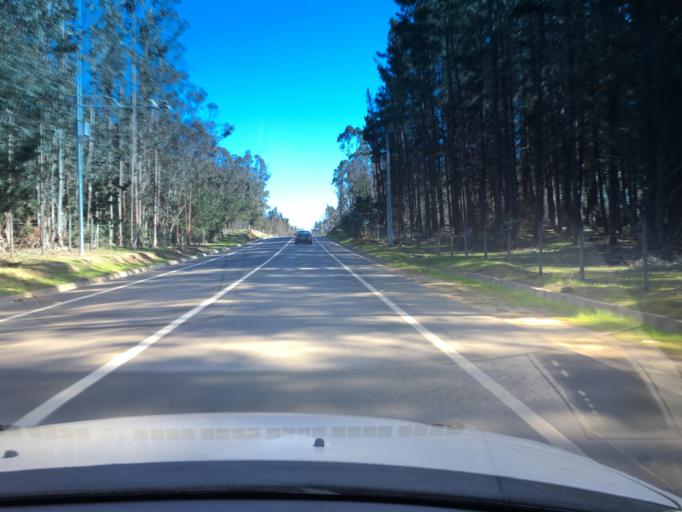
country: CL
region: Valparaiso
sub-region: San Antonio Province
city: El Tabo
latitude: -33.4280
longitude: -71.6407
